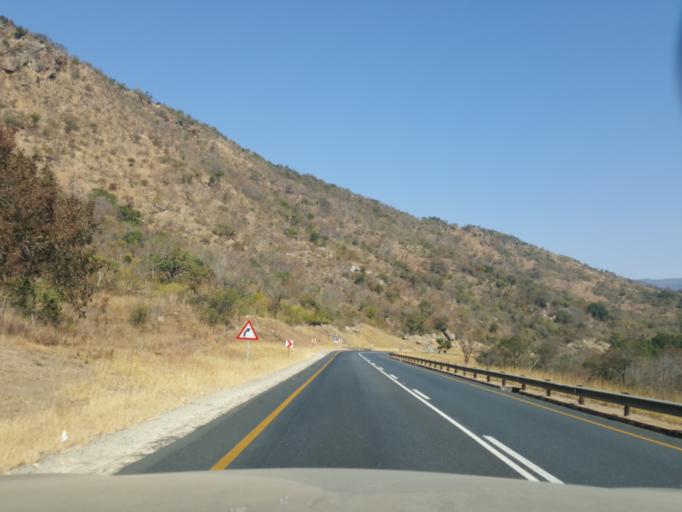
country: ZA
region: Mpumalanga
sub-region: Ehlanzeni District
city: Nelspruit
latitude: -25.4574
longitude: 30.6979
